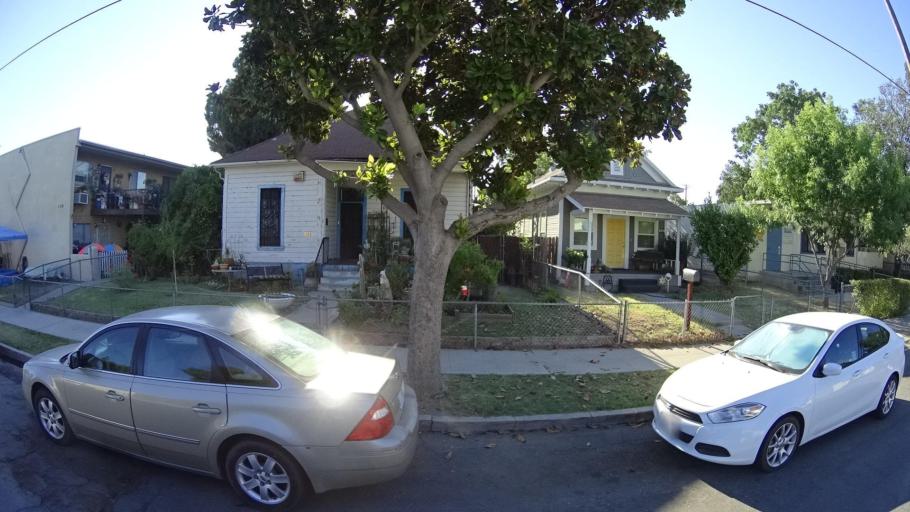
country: US
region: California
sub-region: Fresno County
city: Fresno
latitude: 36.7446
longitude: -119.7958
